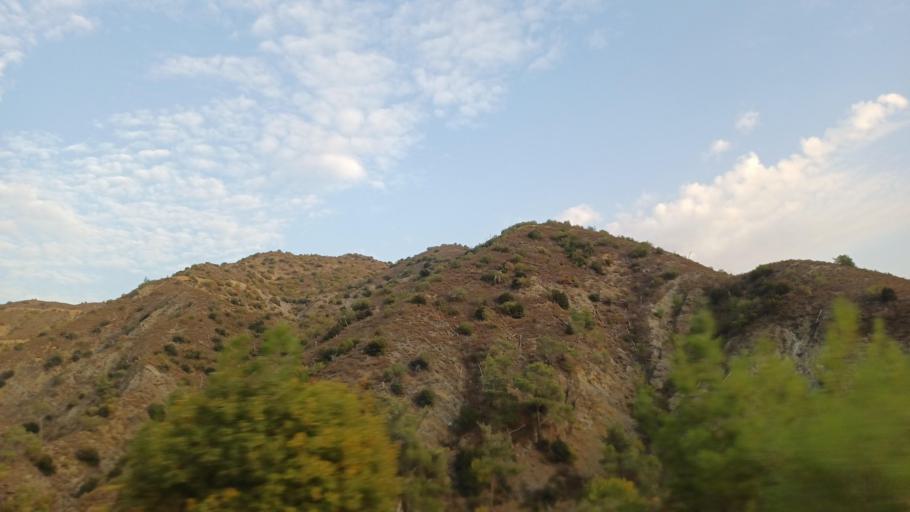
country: CY
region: Limassol
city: Pelendri
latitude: 34.8751
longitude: 32.9197
